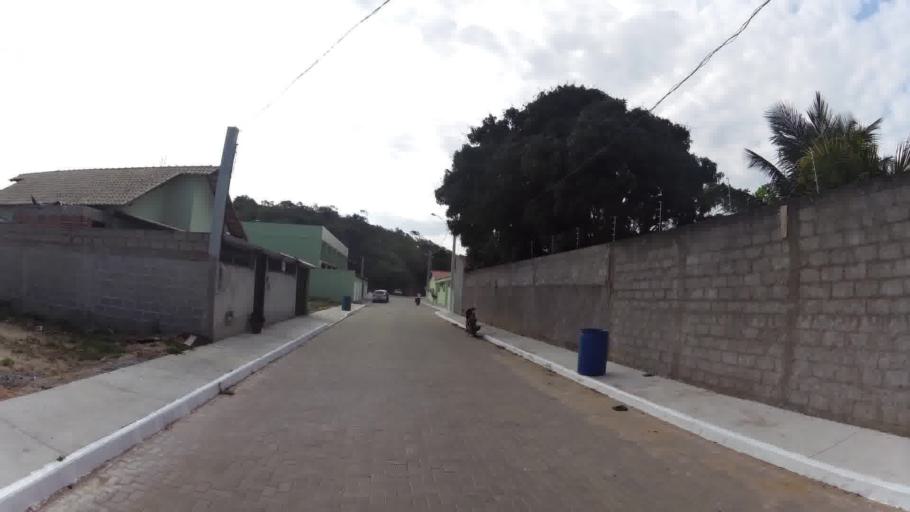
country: BR
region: Espirito Santo
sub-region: Itapemirim
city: Itapemirim
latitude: -21.0078
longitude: -40.8297
